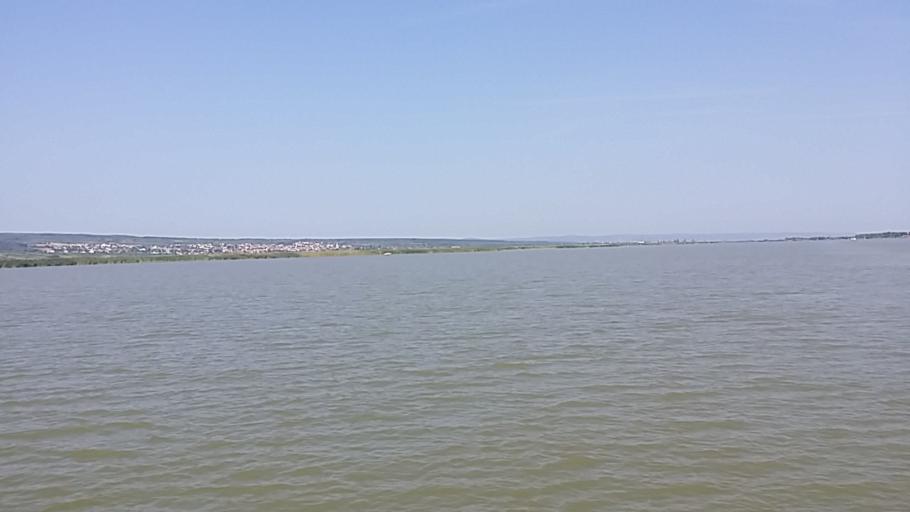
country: AT
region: Burgenland
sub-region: Eisenstadt-Umgebung
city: Morbisch am See
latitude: 47.7262
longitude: 16.6933
